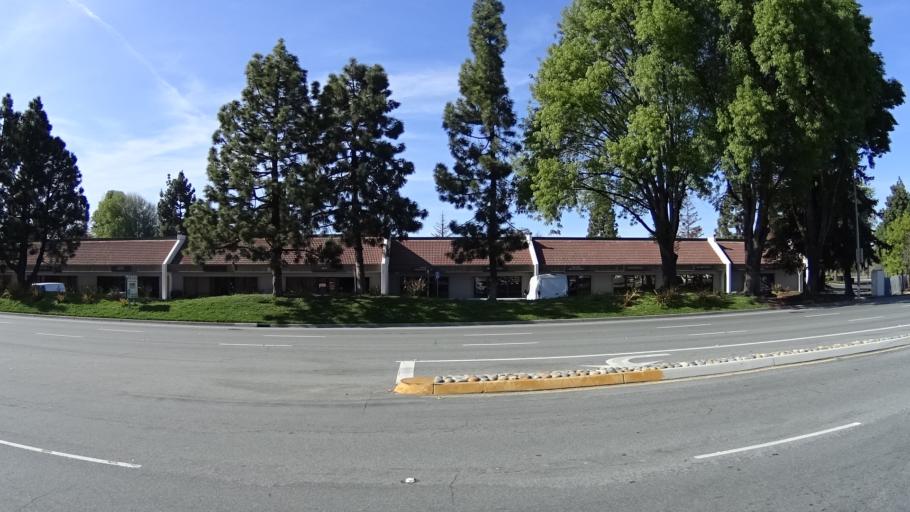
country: US
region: California
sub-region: Santa Clara County
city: San Jose
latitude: 37.3815
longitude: -121.9065
